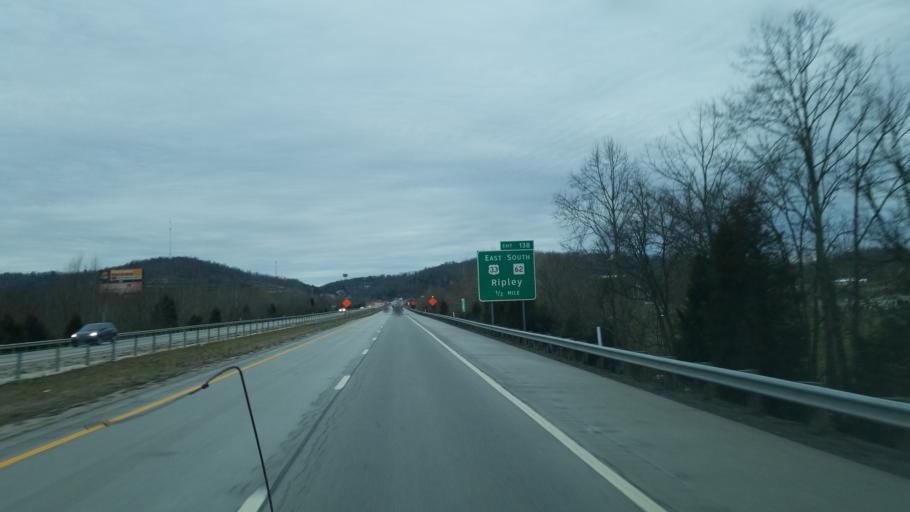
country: US
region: West Virginia
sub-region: Jackson County
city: Ripley
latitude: 38.8304
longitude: -81.7250
